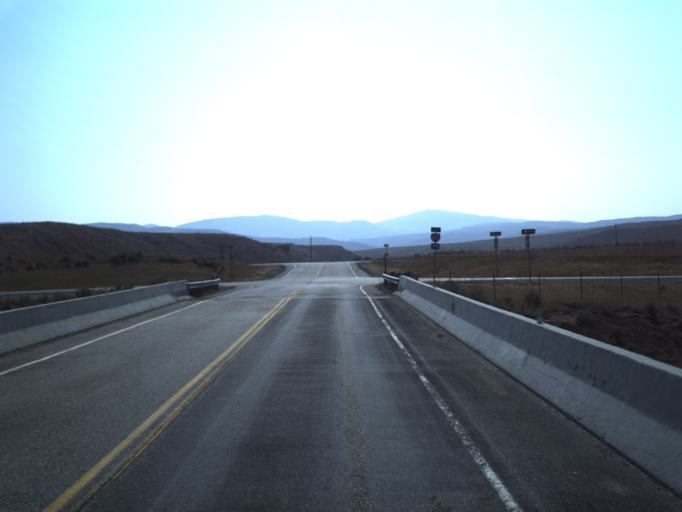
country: US
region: Wyoming
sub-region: Uinta County
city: Evanston
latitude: 41.1193
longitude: -111.1914
